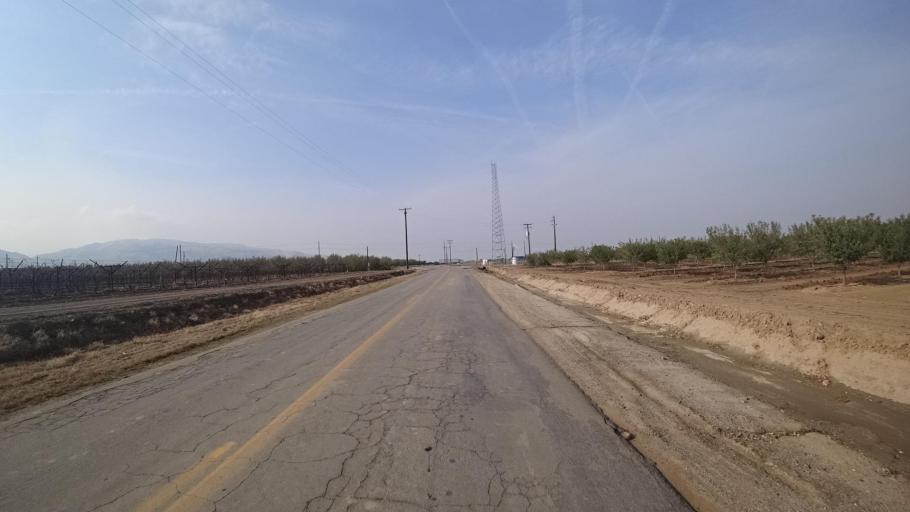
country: US
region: California
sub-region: Kern County
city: Weedpatch
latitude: 35.0340
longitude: -118.9572
